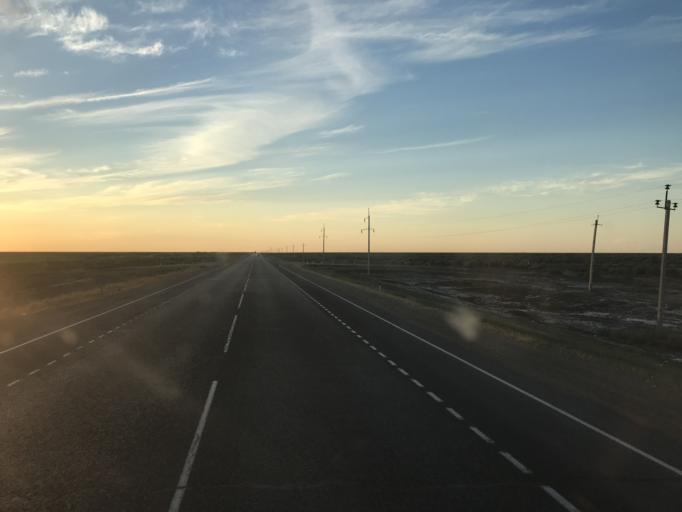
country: KZ
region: Qyzylorda
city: Zhosaly
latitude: 45.2442
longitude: 64.1190
